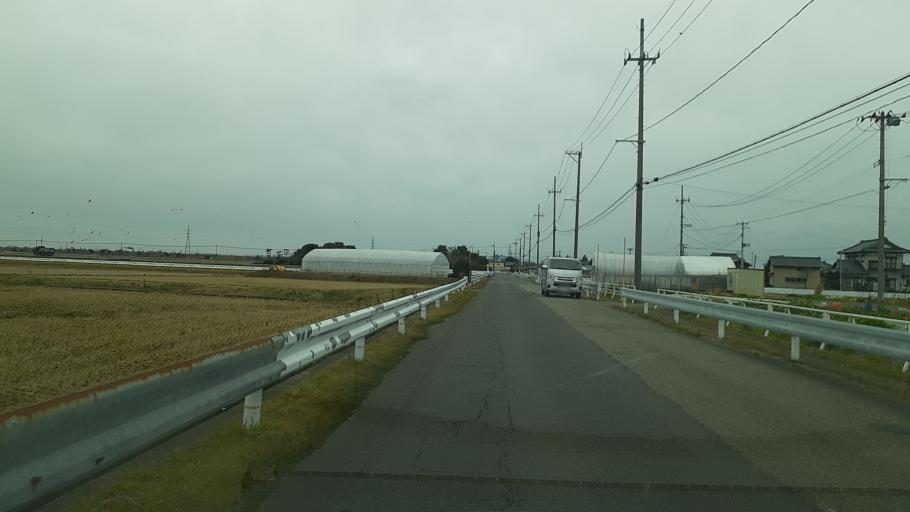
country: JP
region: Niigata
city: Niigata-shi
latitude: 37.8723
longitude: 139.0586
